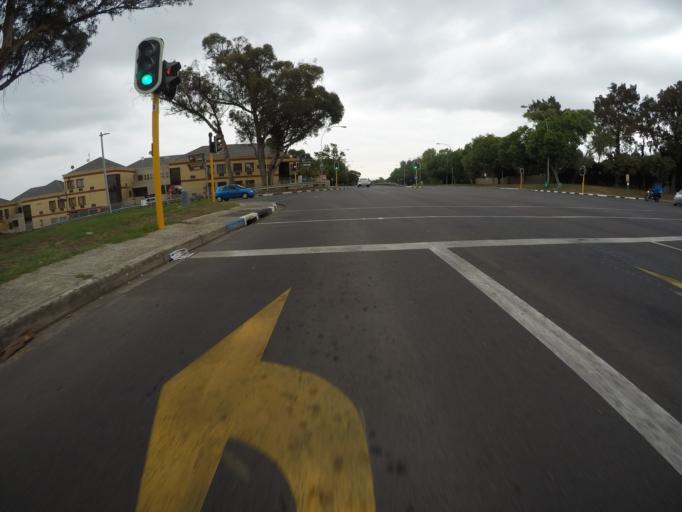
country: ZA
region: Western Cape
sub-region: City of Cape Town
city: Kraaifontein
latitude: -33.8588
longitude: 18.6427
